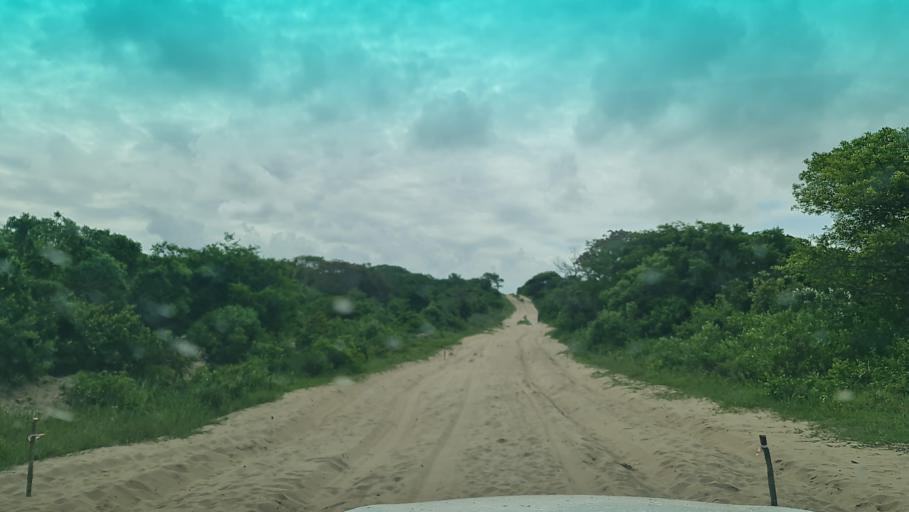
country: MZ
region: Maputo
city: Manhica
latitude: -25.4412
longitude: 32.9317
